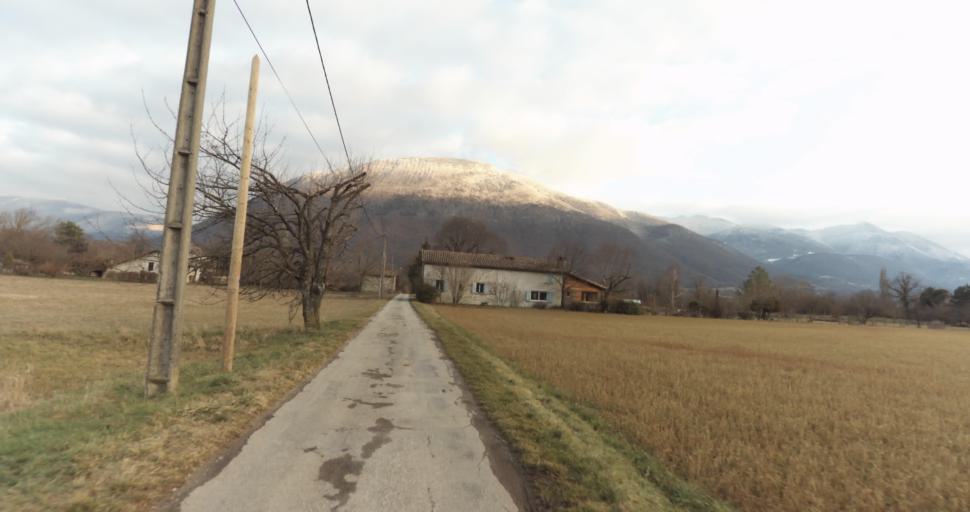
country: FR
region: Rhone-Alpes
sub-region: Departement de l'Isere
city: Vif
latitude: 45.0669
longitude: 5.6994
